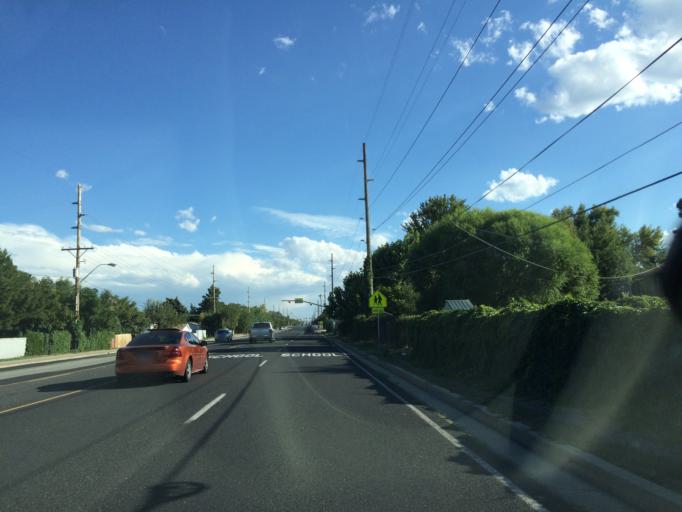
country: US
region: Utah
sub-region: Salt Lake County
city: Taylorsville
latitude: 40.6871
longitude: -111.9580
